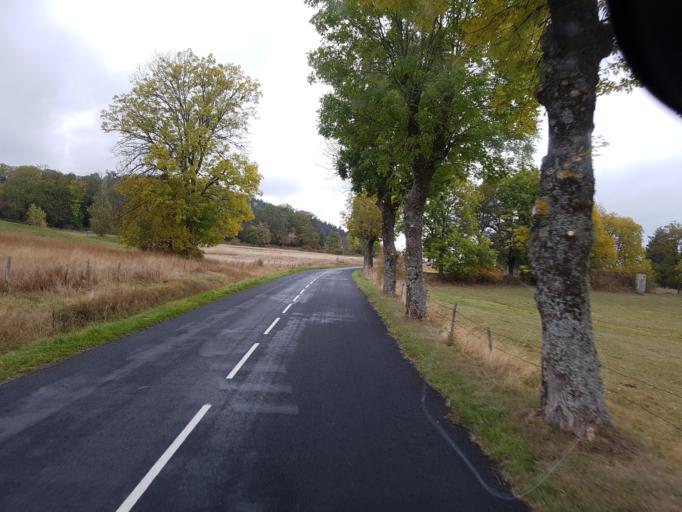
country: FR
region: Languedoc-Roussillon
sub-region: Departement de la Lozere
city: Langogne
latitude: 44.7186
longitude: 3.8270
